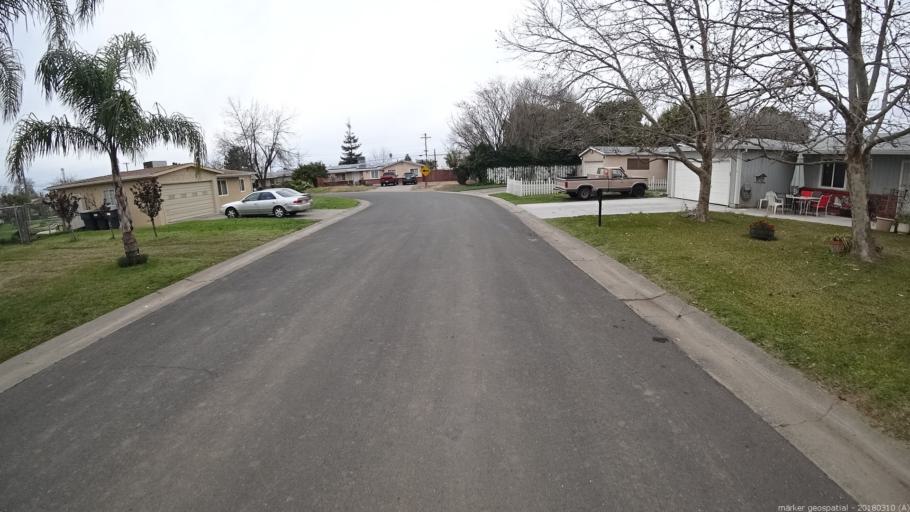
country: US
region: California
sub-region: Sacramento County
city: Florin
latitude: 38.4948
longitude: -121.4057
